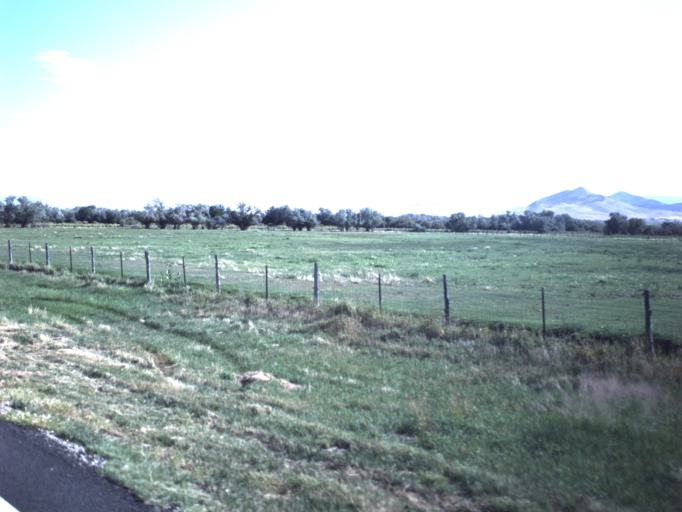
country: US
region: Utah
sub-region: Sevier County
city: Salina
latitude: 38.9868
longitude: -111.8607
